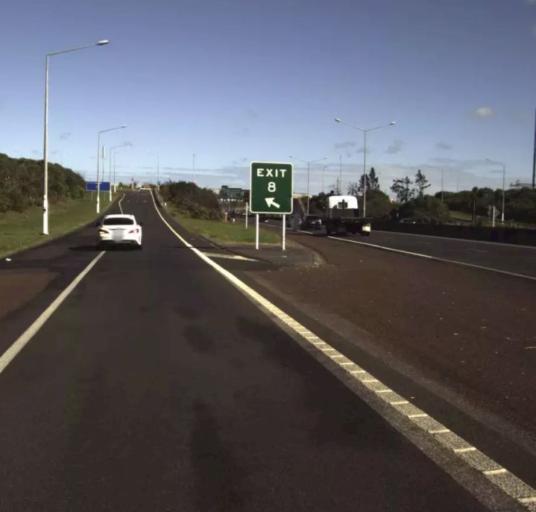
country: NZ
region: Auckland
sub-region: Auckland
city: Rosebank
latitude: -36.7892
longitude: 174.6579
